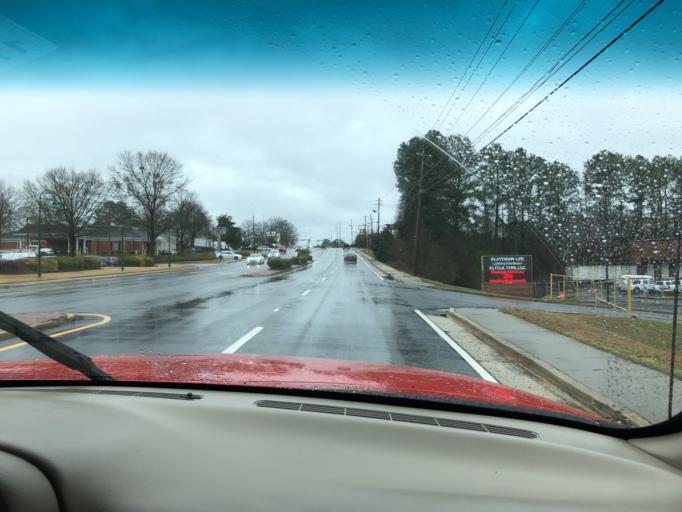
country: US
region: Georgia
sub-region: Clayton County
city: Morrow
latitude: 33.5716
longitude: -84.3527
